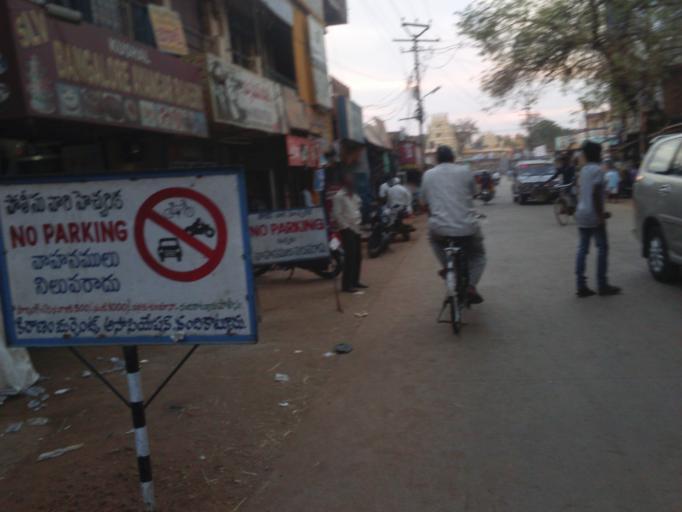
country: IN
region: Andhra Pradesh
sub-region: Kurnool
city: Nandikotkur
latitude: 15.8556
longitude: 78.2640
